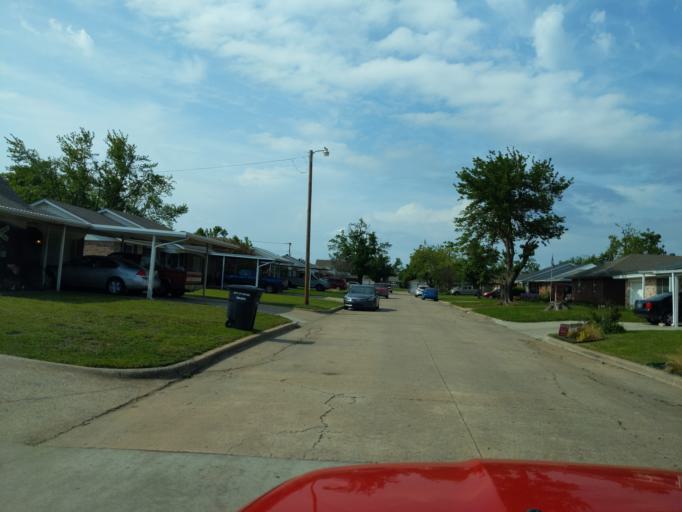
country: US
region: Oklahoma
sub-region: Cleveland County
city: Moore
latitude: 35.3496
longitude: -97.4998
